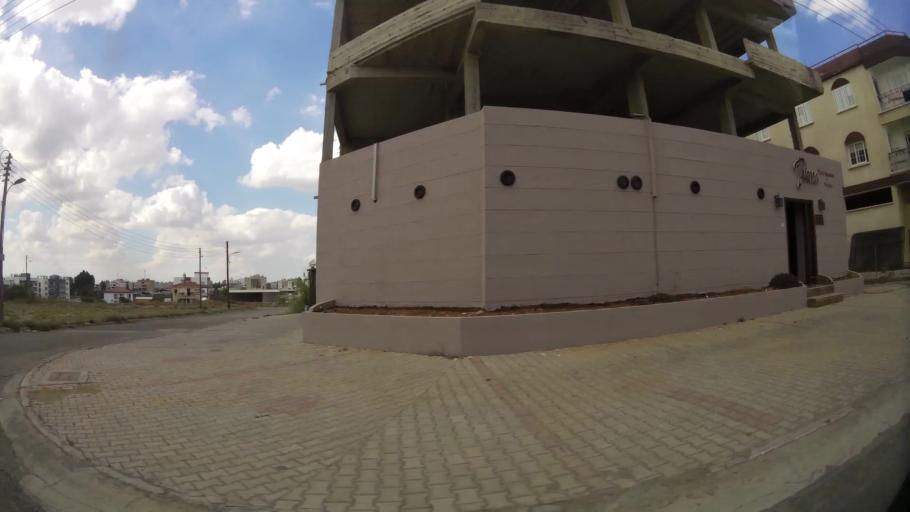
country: CY
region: Lefkosia
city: Nicosia
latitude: 35.2093
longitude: 33.3721
